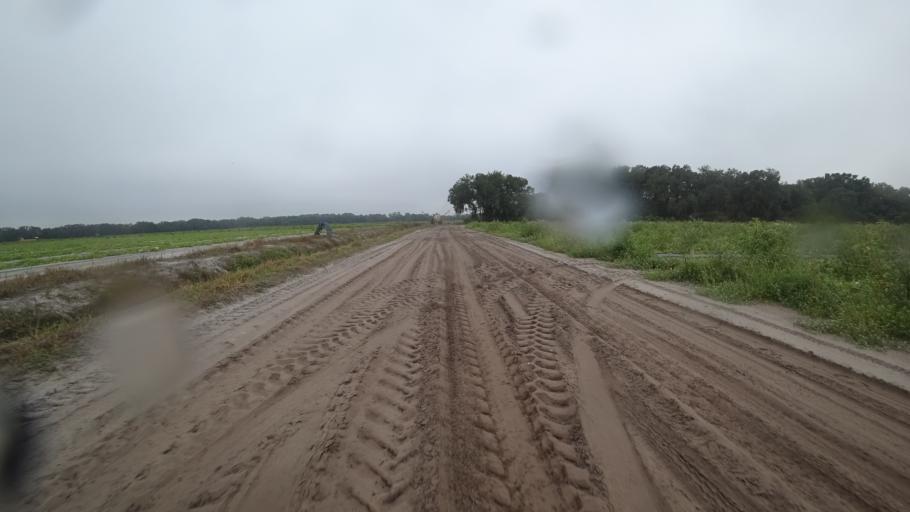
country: US
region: Florida
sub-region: Sarasota County
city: Warm Mineral Springs
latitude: 27.2862
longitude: -82.1583
